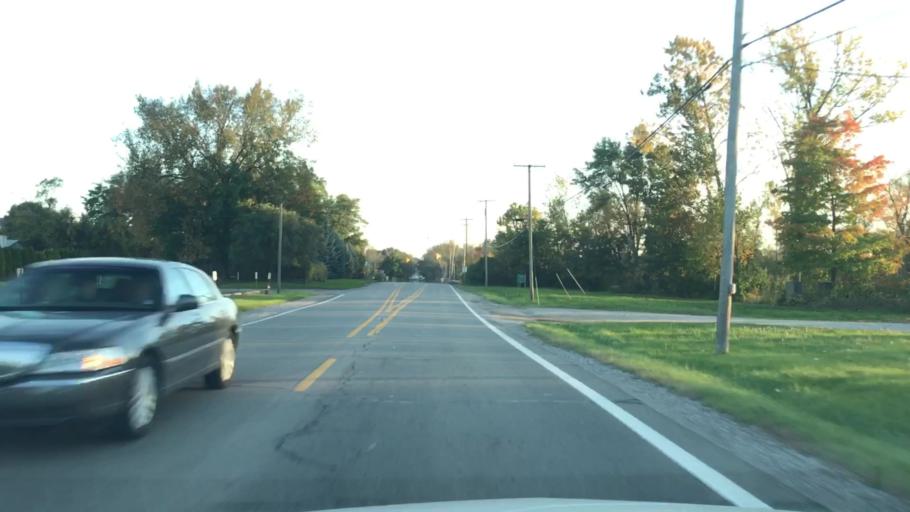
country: US
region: Michigan
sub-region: Macomb County
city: Shelby
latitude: 42.6645
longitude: -83.0735
